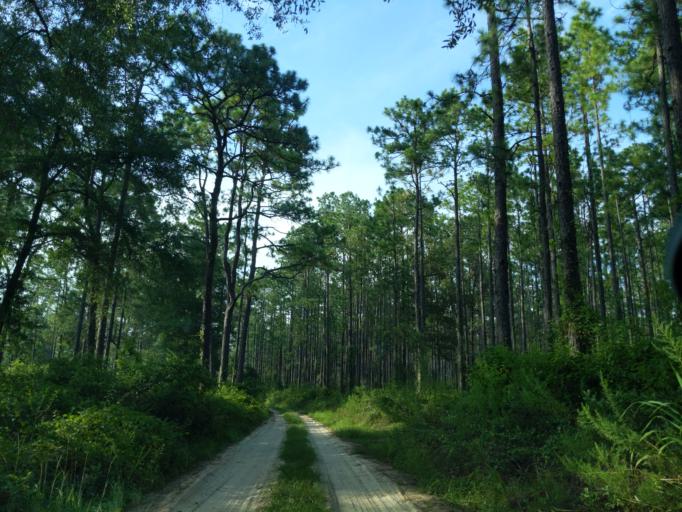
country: US
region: Florida
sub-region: Leon County
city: Tallahassee
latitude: 30.3525
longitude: -84.3607
